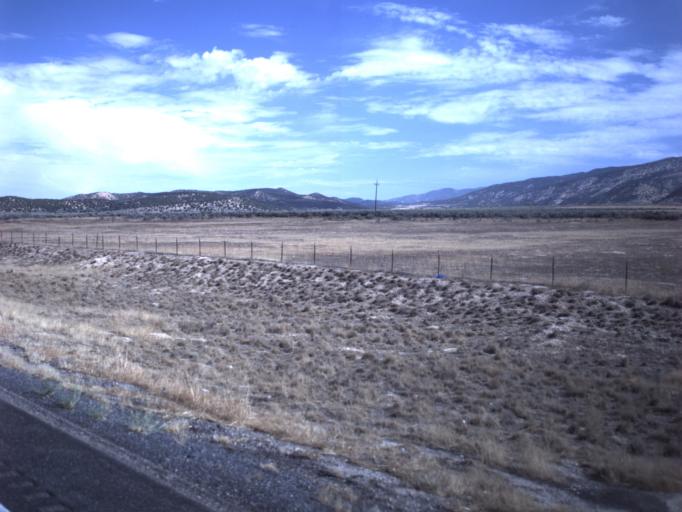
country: US
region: Utah
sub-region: Sanpete County
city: Gunnison
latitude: 39.3077
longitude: -111.8983
